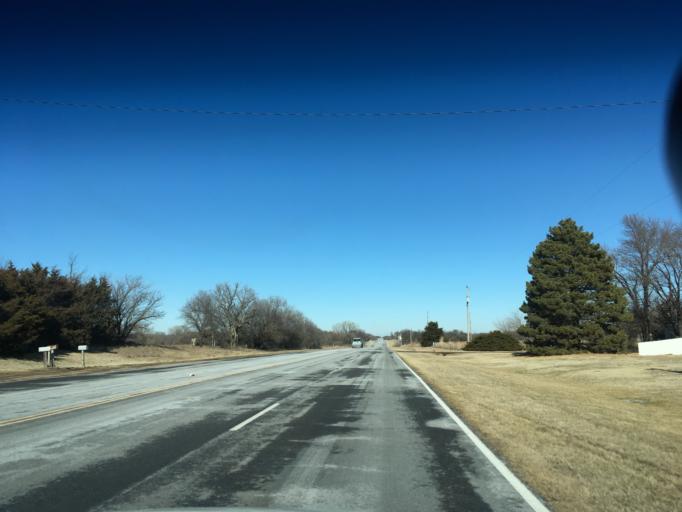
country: US
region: Kansas
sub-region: Harvey County
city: Sedgwick
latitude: 37.9285
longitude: -97.3363
